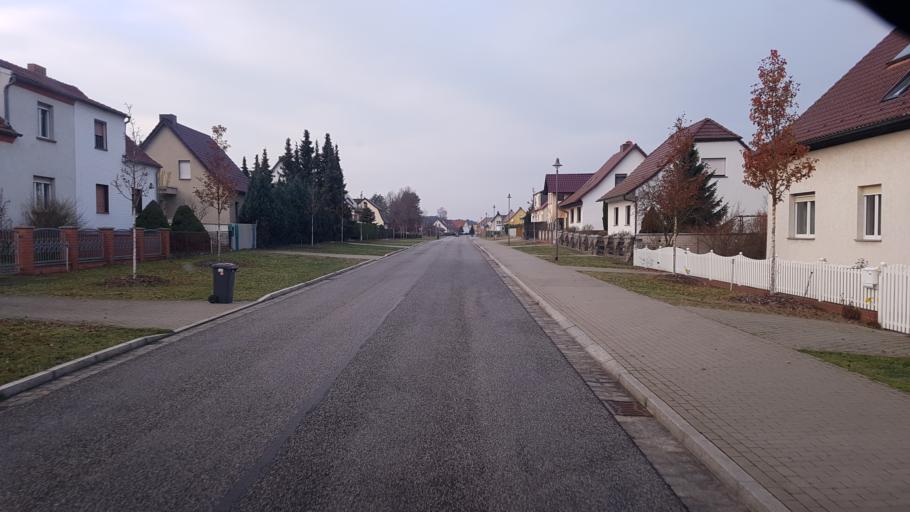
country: DE
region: Brandenburg
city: Ziltendorf
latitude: 52.2012
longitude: 14.6317
